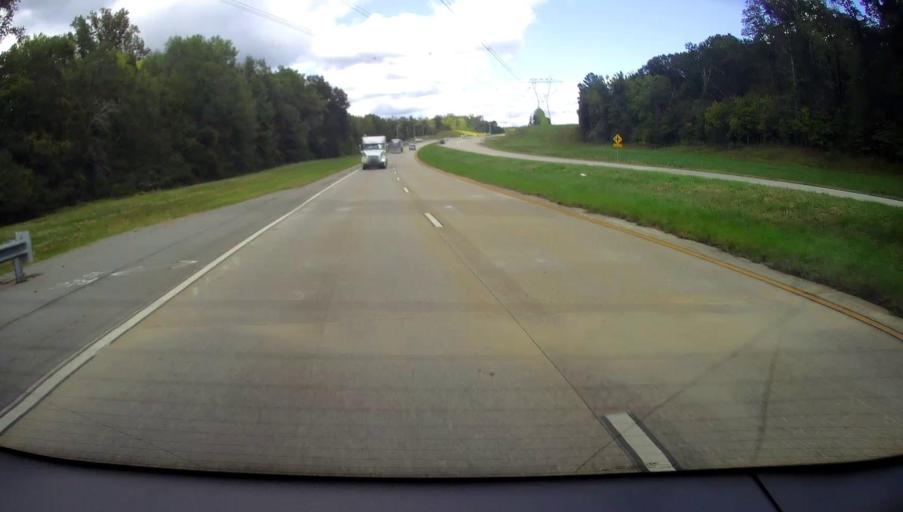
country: US
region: Georgia
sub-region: Jones County
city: Gray
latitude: 33.0158
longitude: -83.5685
